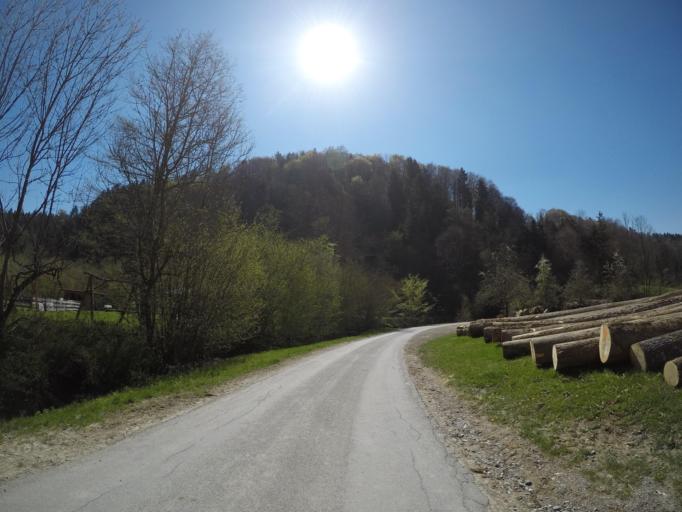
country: DE
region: Baden-Wuerttemberg
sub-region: Tuebingen Region
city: Horgenzell
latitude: 47.7861
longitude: 9.4428
